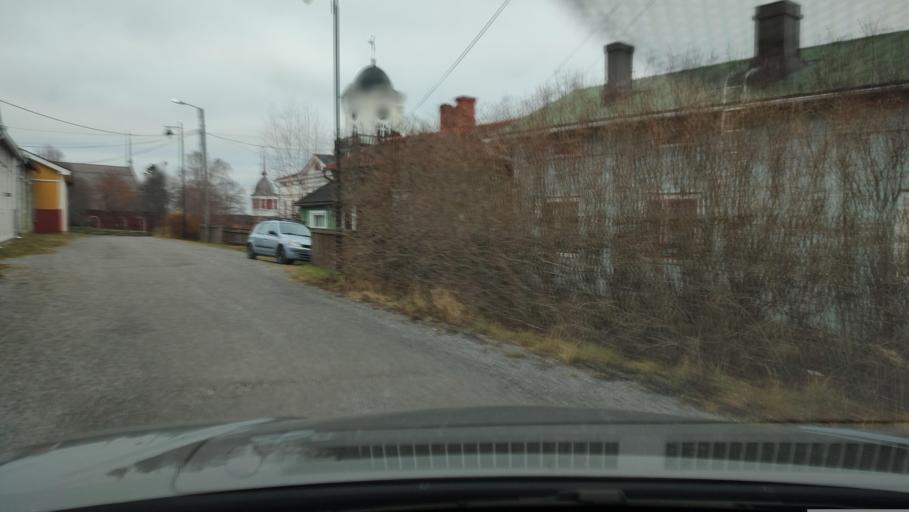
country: FI
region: Ostrobothnia
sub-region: Sydosterbotten
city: Kristinestad
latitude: 62.2736
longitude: 21.3724
